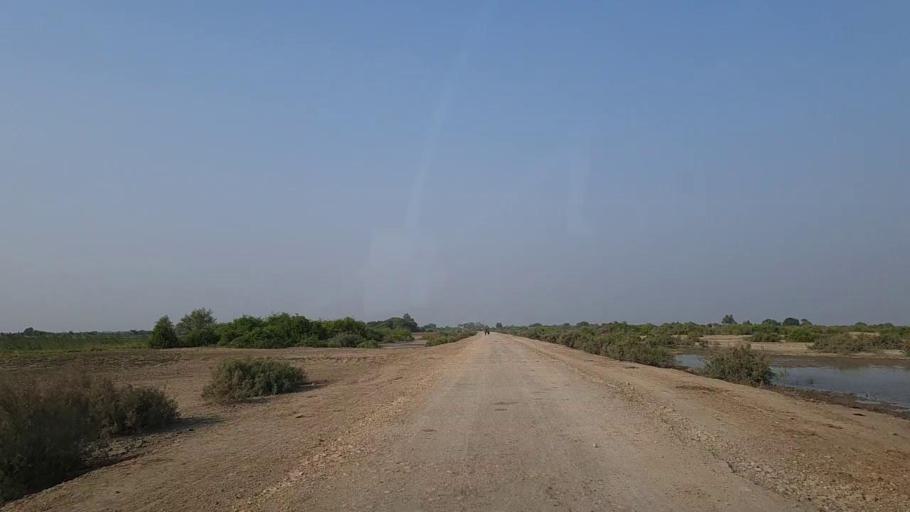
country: PK
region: Sindh
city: Mirpur Sakro
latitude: 24.6394
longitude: 67.7674
